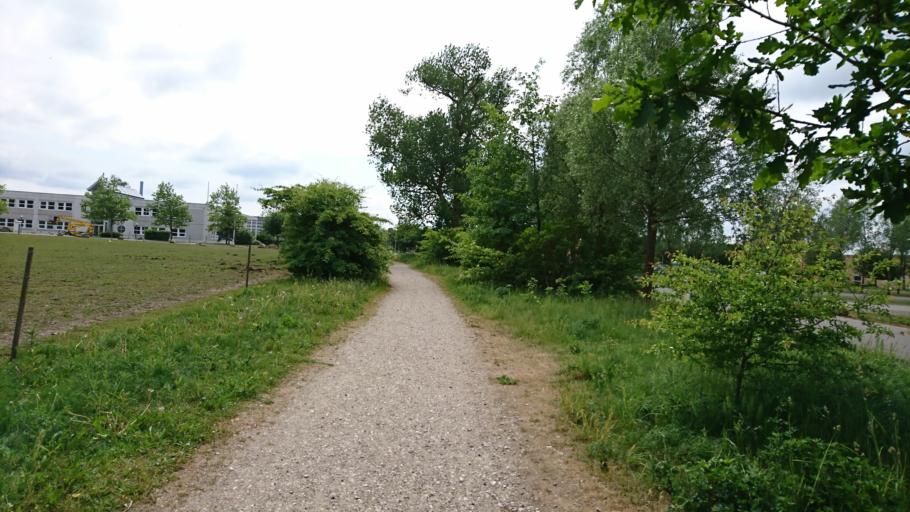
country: DK
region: Capital Region
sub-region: Ballerup Kommune
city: Malov
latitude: 55.7319
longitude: 12.3364
